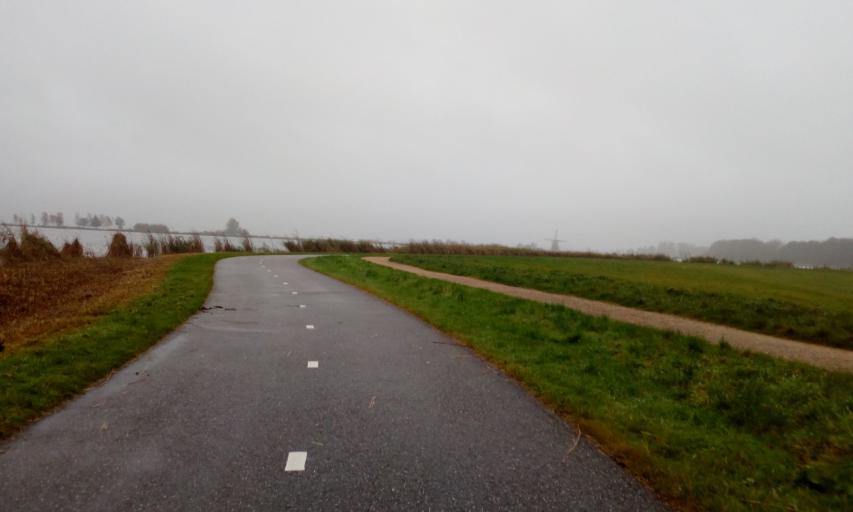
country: NL
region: South Holland
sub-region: Gemeente Lansingerland
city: Bleiswijk
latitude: 52.0105
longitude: 4.5550
